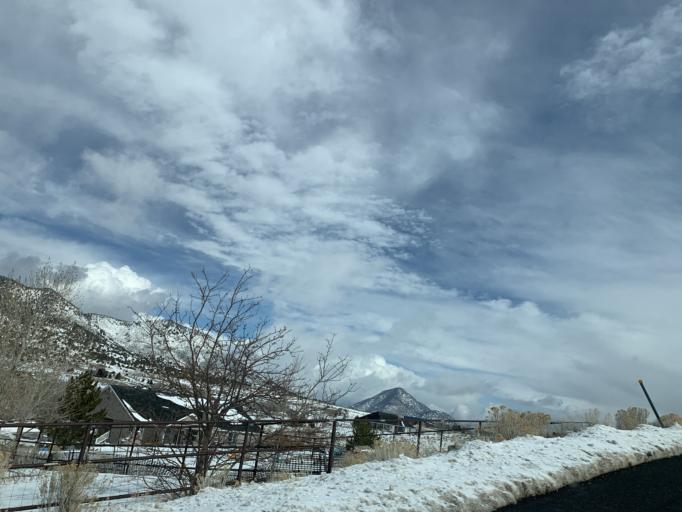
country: US
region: Utah
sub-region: Utah County
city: Genola
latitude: 39.9534
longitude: -112.1119
